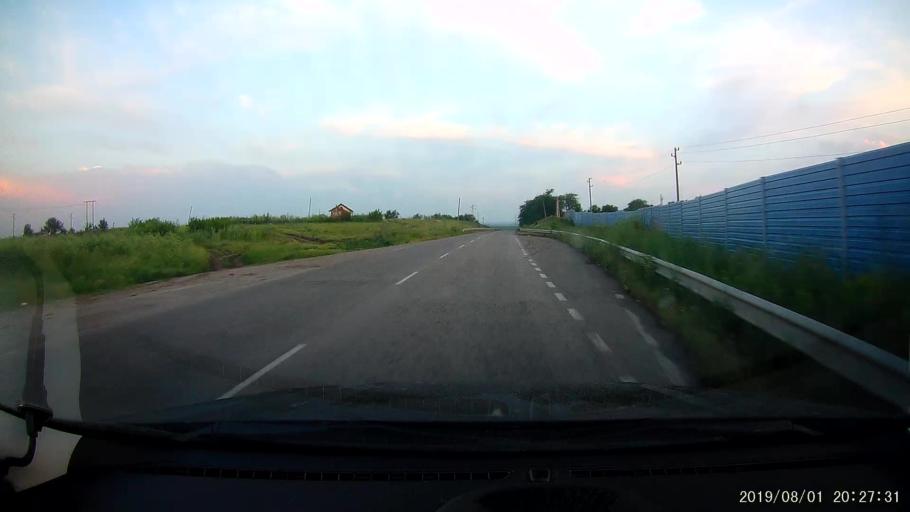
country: BG
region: Yambol
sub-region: Obshtina Elkhovo
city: Elkhovo
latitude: 42.1789
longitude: 26.5844
